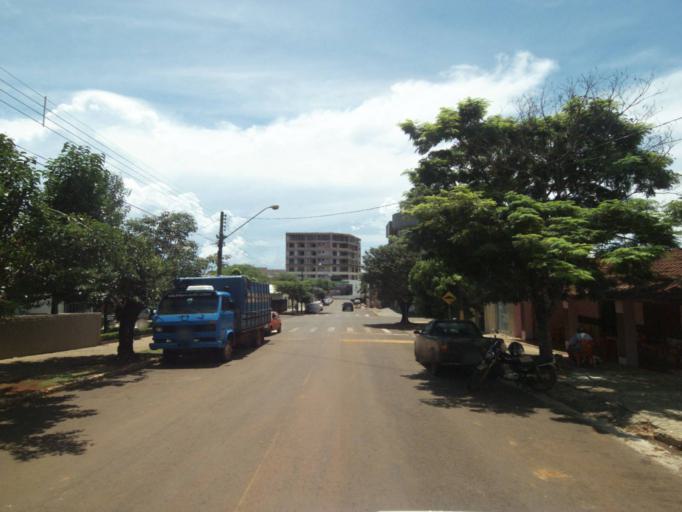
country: BR
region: Parana
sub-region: Guaraniacu
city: Guaraniacu
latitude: -25.0991
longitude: -52.8675
